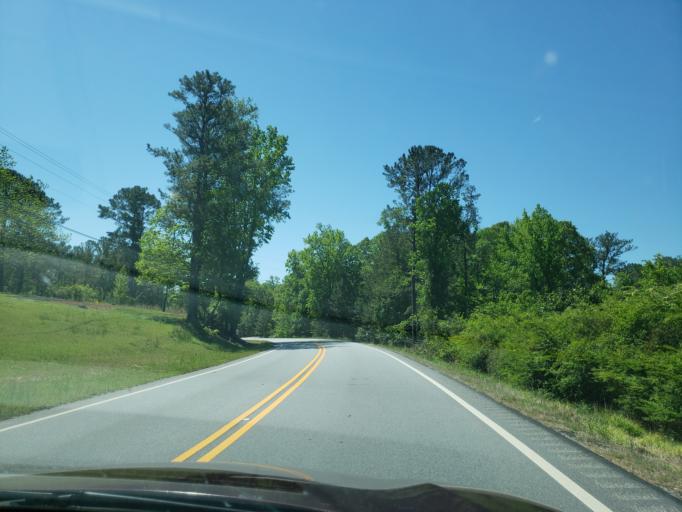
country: US
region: Alabama
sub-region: Tallapoosa County
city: Dadeville
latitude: 32.6968
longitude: -85.7877
